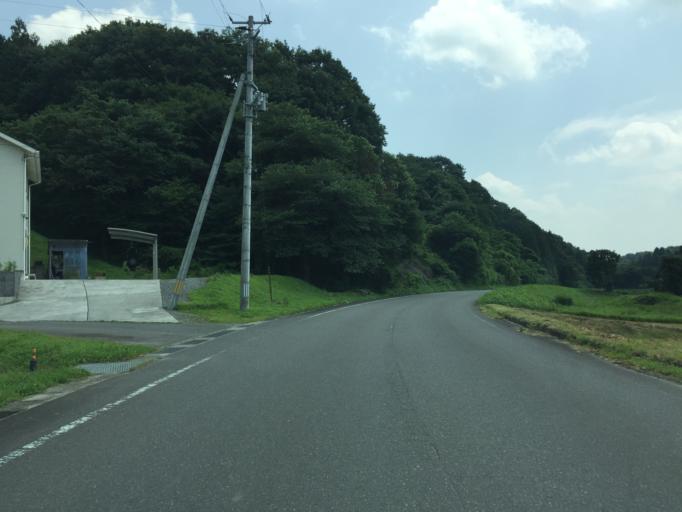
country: JP
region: Fukushima
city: Ishikawa
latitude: 37.2259
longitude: 140.5569
